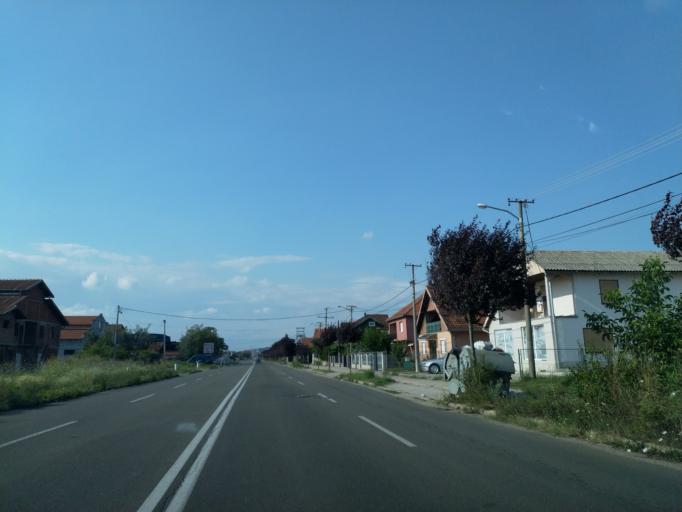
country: RS
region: Central Serbia
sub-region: Pomoravski Okrug
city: Paracin
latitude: 43.8404
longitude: 21.4152
